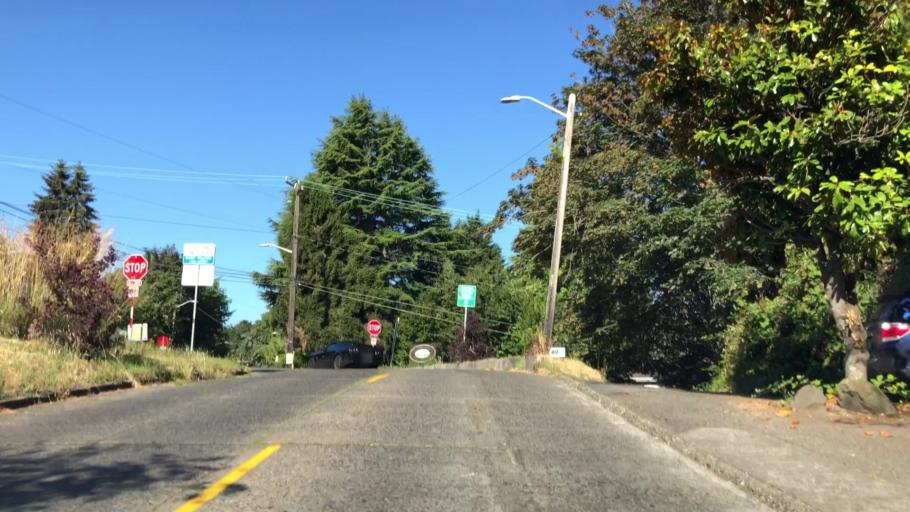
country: US
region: Washington
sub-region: King County
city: Seattle
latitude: 47.6432
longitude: -122.3491
